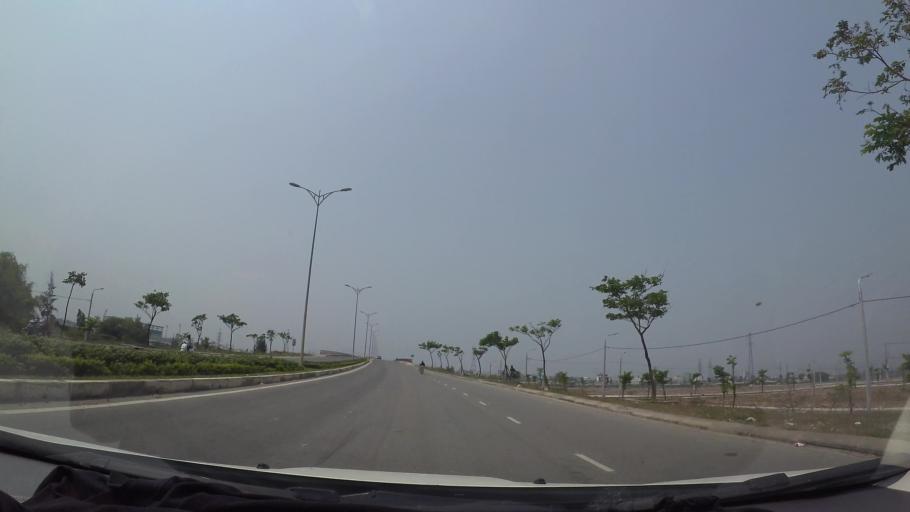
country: VN
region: Da Nang
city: Ngu Hanh Son
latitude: 16.0002
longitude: 108.2322
